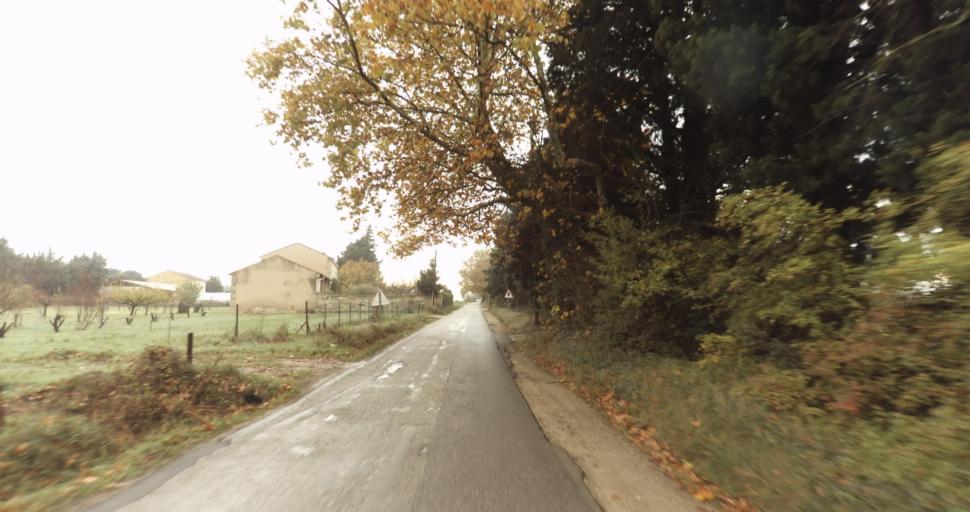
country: FR
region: Provence-Alpes-Cote d'Azur
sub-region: Departement des Bouches-du-Rhone
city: Rognonas
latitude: 43.8920
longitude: 4.8005
